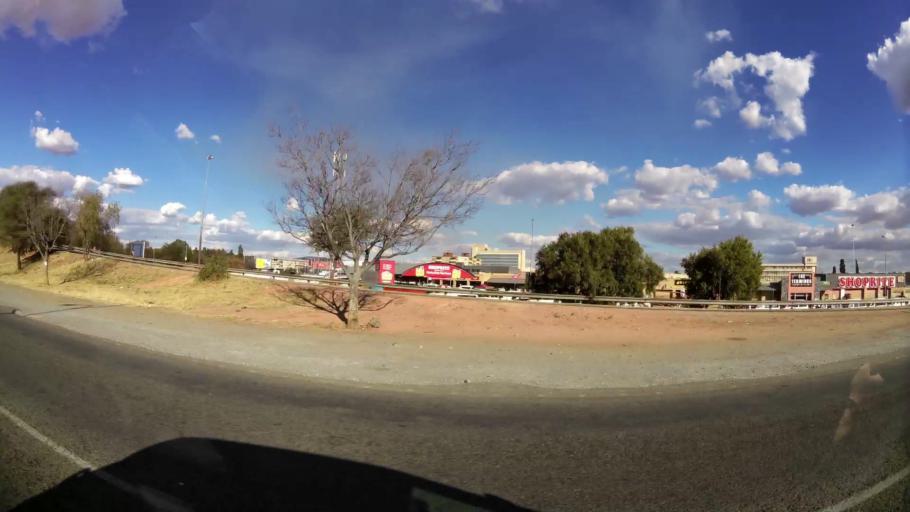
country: ZA
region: North-West
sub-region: Dr Kenneth Kaunda District Municipality
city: Klerksdorp
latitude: -26.8614
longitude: 26.6632
